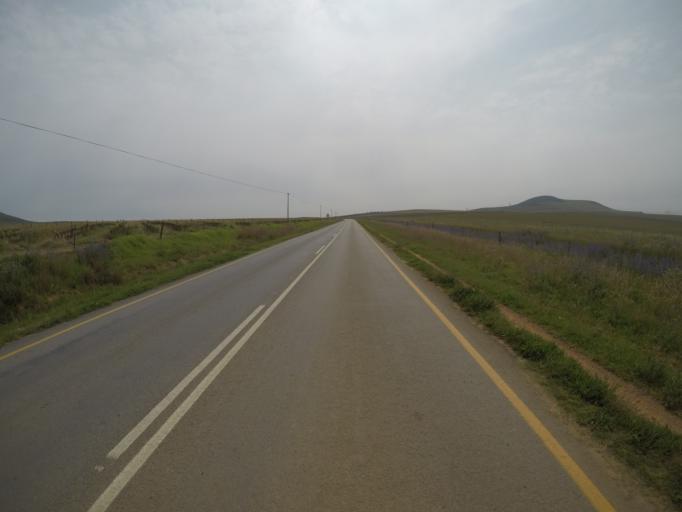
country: ZA
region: Western Cape
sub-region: City of Cape Town
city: Kraaifontein
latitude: -33.7878
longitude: 18.6446
